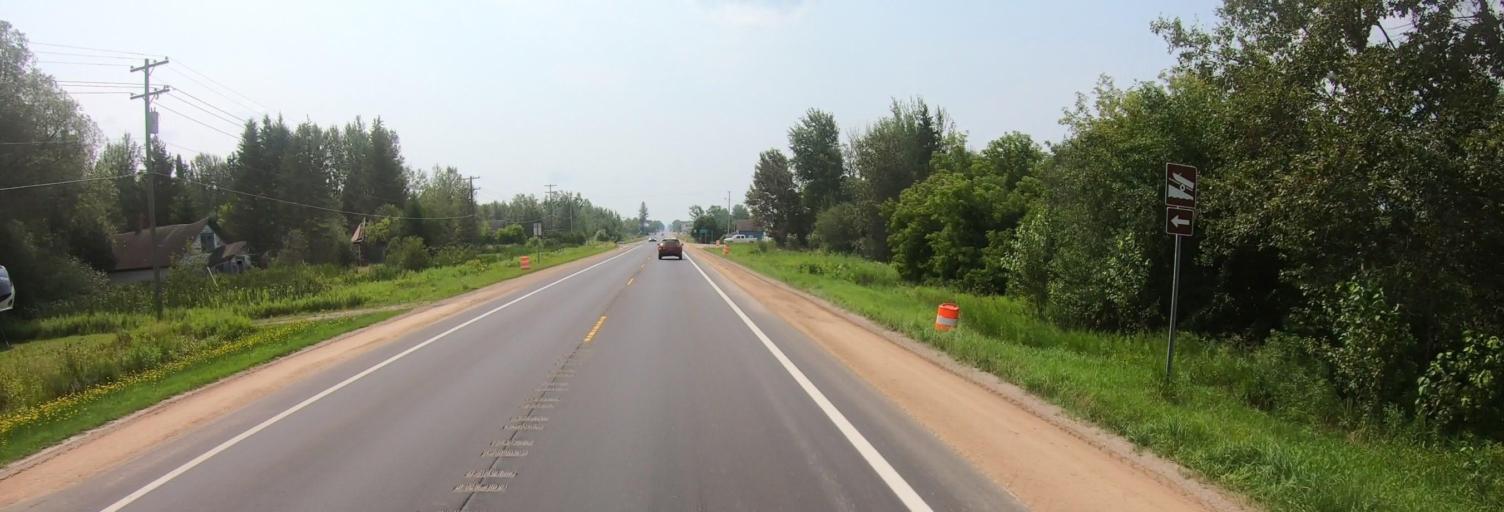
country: US
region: Michigan
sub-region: Luce County
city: Newberry
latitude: 46.3625
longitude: -85.5099
